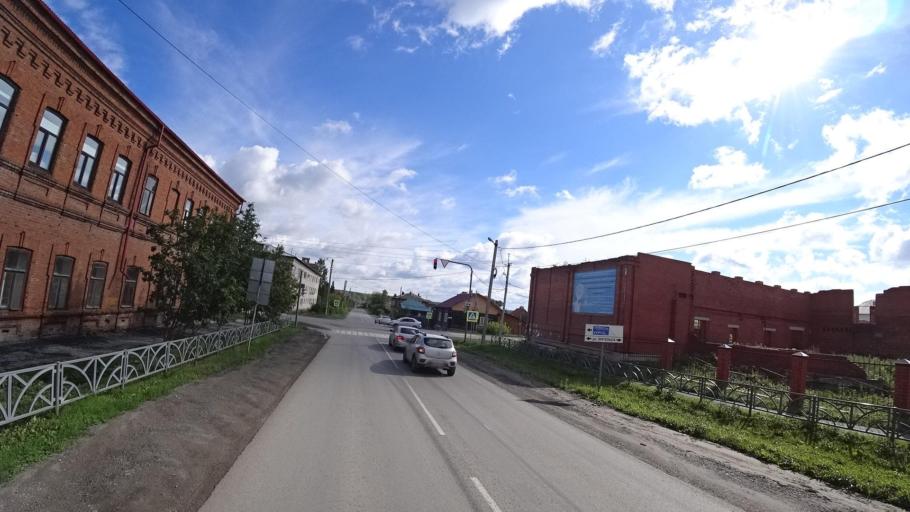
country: RU
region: Sverdlovsk
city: Kamyshlov
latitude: 56.8450
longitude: 62.6985
